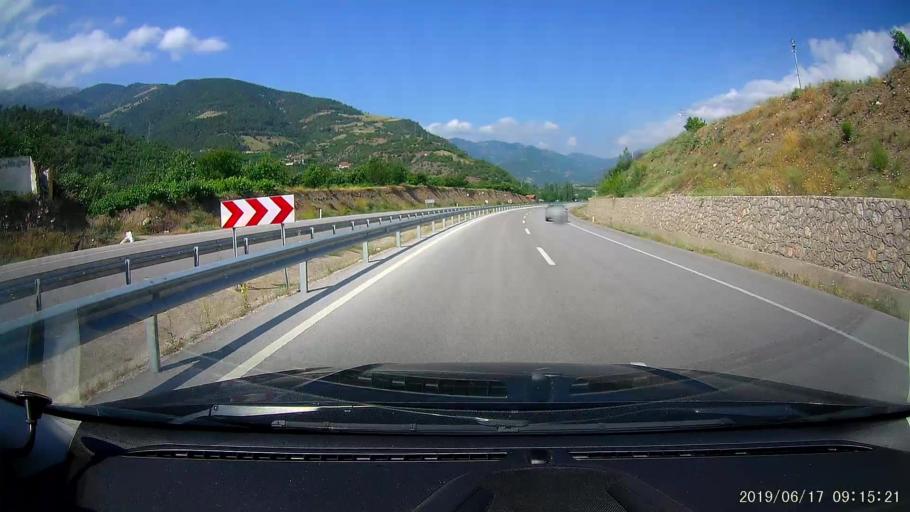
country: TR
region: Amasya
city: Akdag
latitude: 40.7472
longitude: 36.0386
